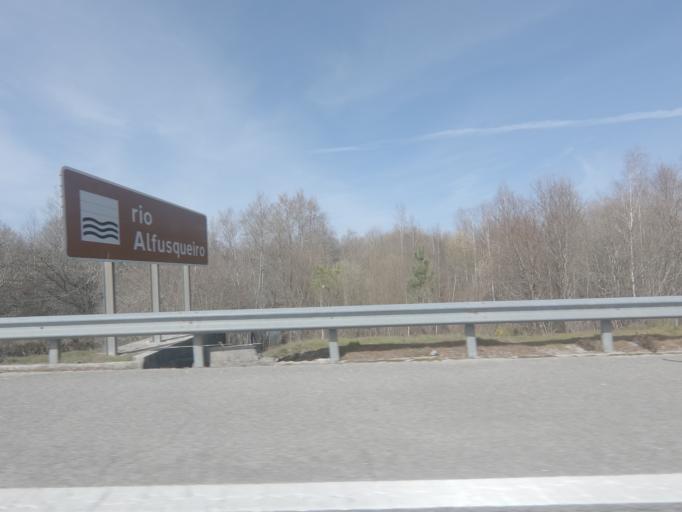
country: PT
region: Viseu
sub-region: Oliveira de Frades
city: Oliveira de Frades
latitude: 40.6854
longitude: -8.2191
